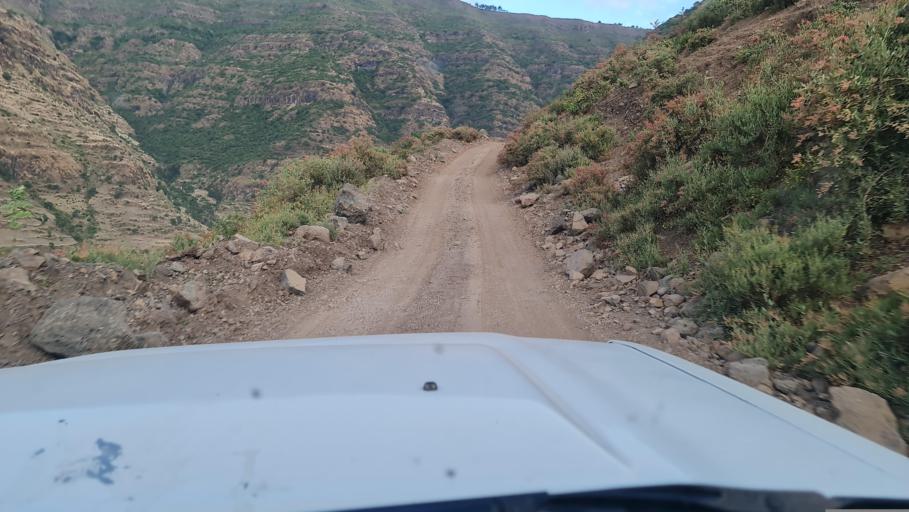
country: ET
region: Amhara
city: Debark'
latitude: 13.0150
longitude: 38.0530
